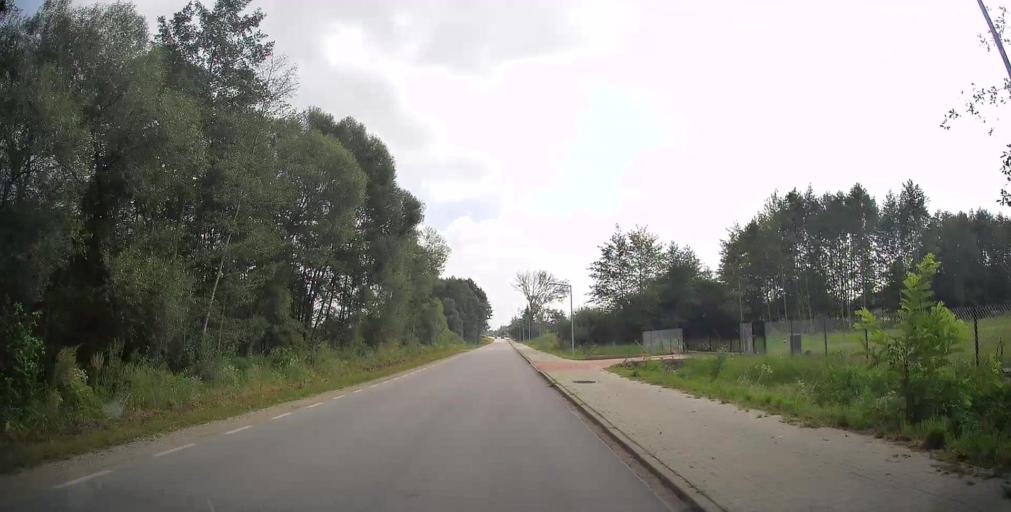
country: PL
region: Masovian Voivodeship
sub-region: Powiat bialobrzeski
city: Sucha
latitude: 51.6135
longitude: 20.9656
